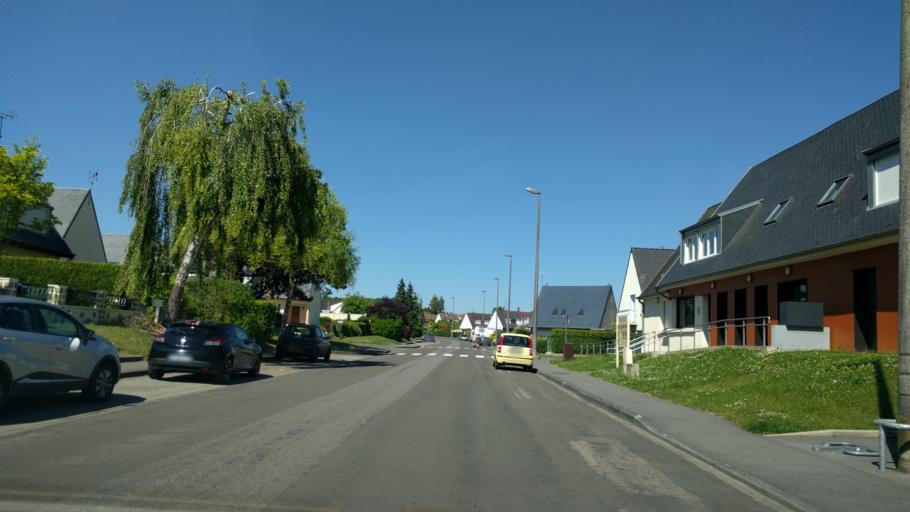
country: FR
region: Picardie
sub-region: Departement de la Somme
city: Peronne
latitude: 49.9388
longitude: 2.9363
